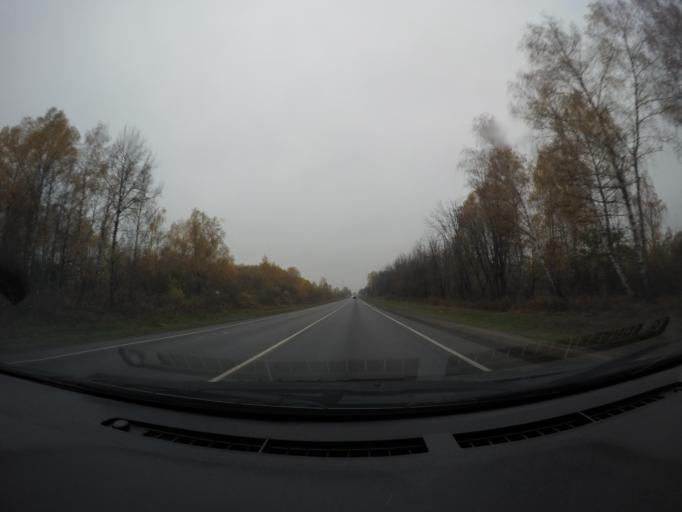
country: RU
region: Moskovskaya
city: Yakovlevskoye
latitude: 55.3667
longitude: 38.0541
